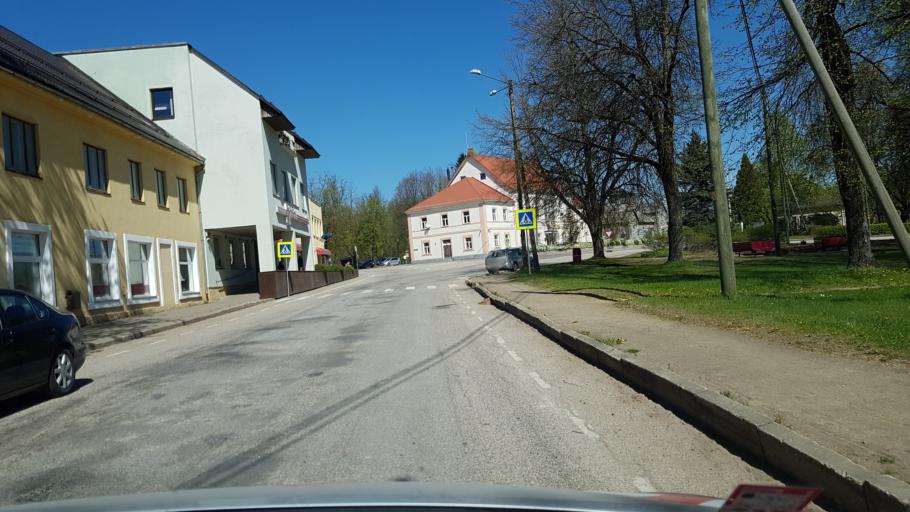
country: EE
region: Vorumaa
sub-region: Antsla vald
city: Vana-Antsla
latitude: 57.8285
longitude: 26.5273
